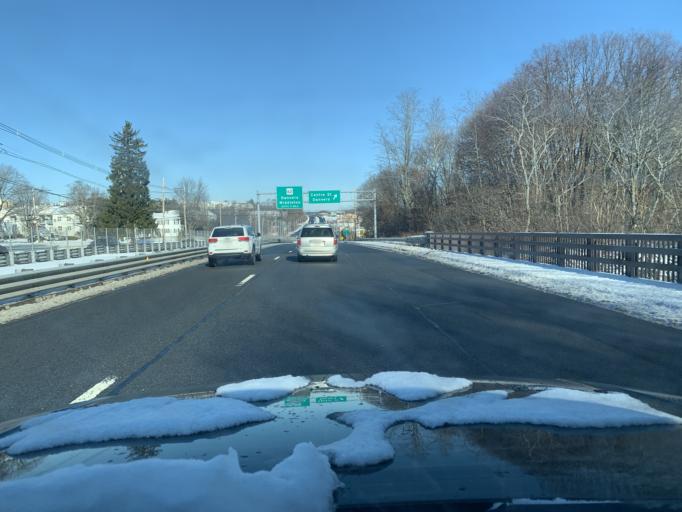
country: US
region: Massachusetts
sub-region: Essex County
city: Danvers
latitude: 42.5691
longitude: -70.9736
